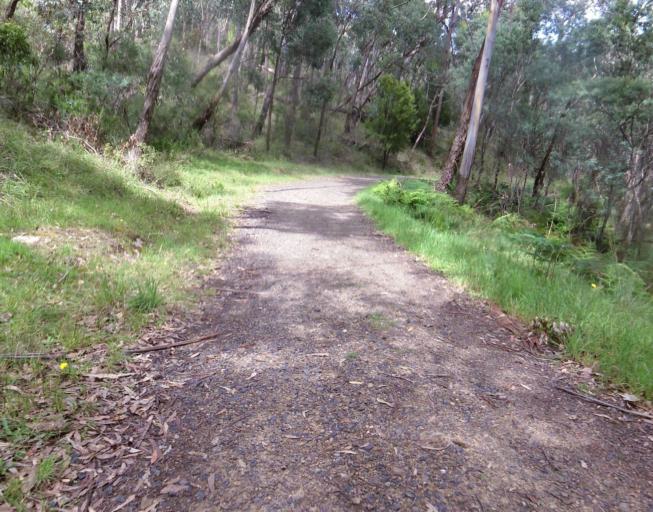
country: AU
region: Victoria
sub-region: Yarra Ranges
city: Montrose
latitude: -37.8266
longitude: 145.3440
